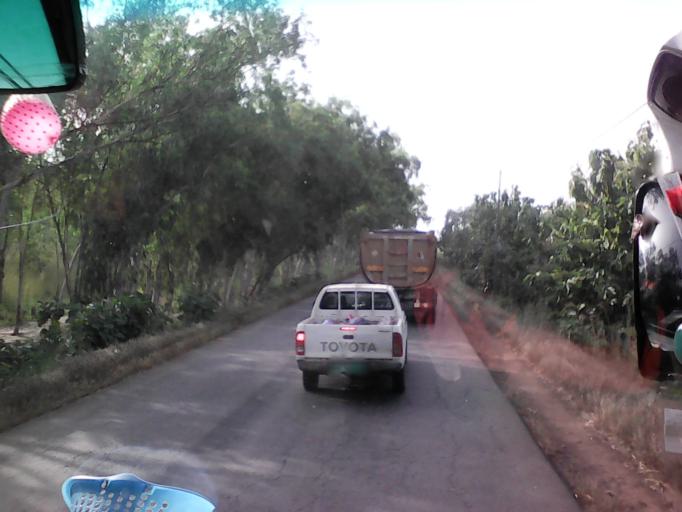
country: TG
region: Kara
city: Kara
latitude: 9.4808
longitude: 1.2097
